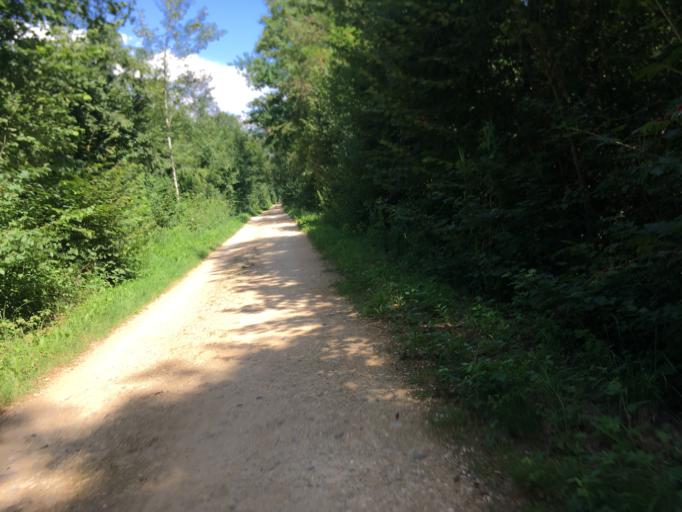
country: CH
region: Fribourg
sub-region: See District
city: Bas-Vully
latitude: 46.9555
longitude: 7.1264
